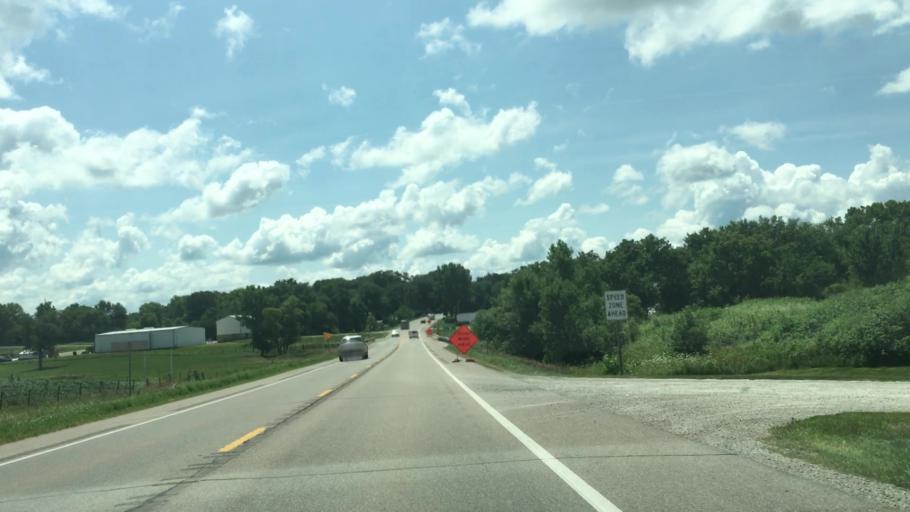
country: US
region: Iowa
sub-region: Johnson County
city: Solon
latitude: 41.8138
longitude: -91.4947
